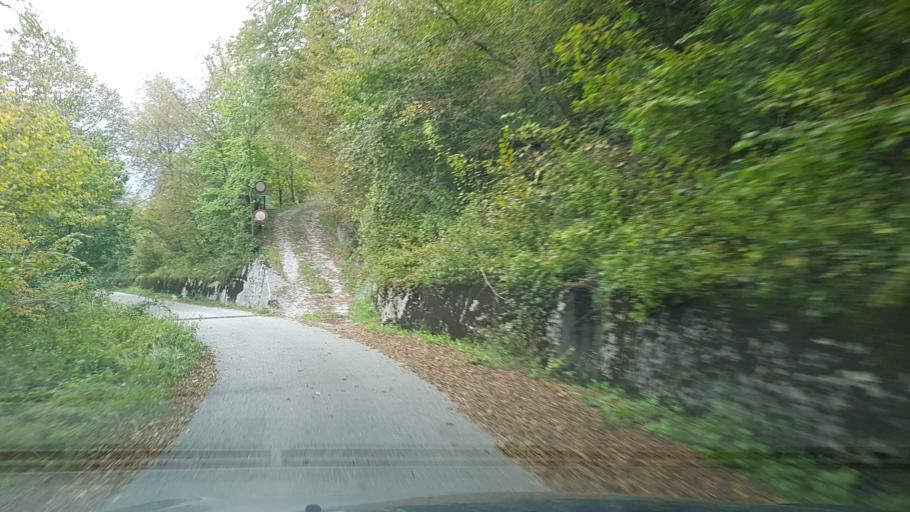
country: IT
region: Friuli Venezia Giulia
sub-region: Provincia di Udine
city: Venzone
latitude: 46.3345
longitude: 13.1758
